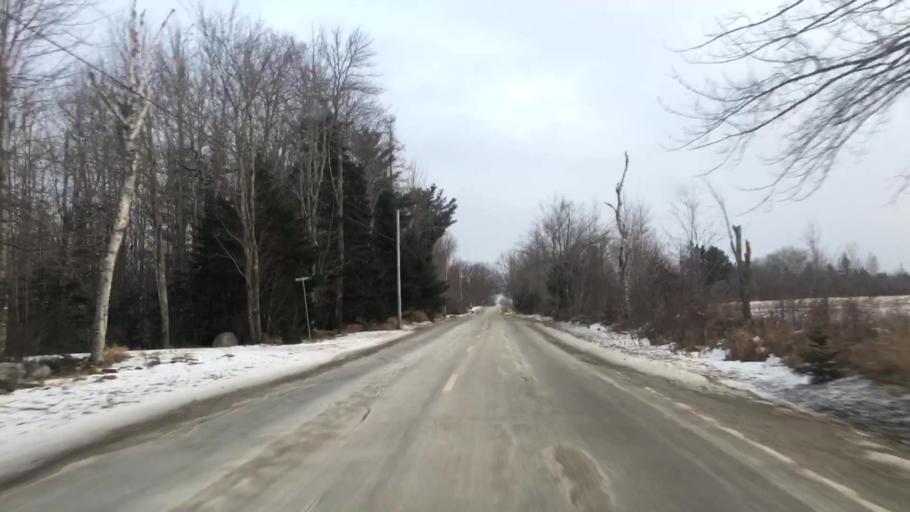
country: US
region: Maine
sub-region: Hancock County
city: Franklin
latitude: 44.7047
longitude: -68.3409
